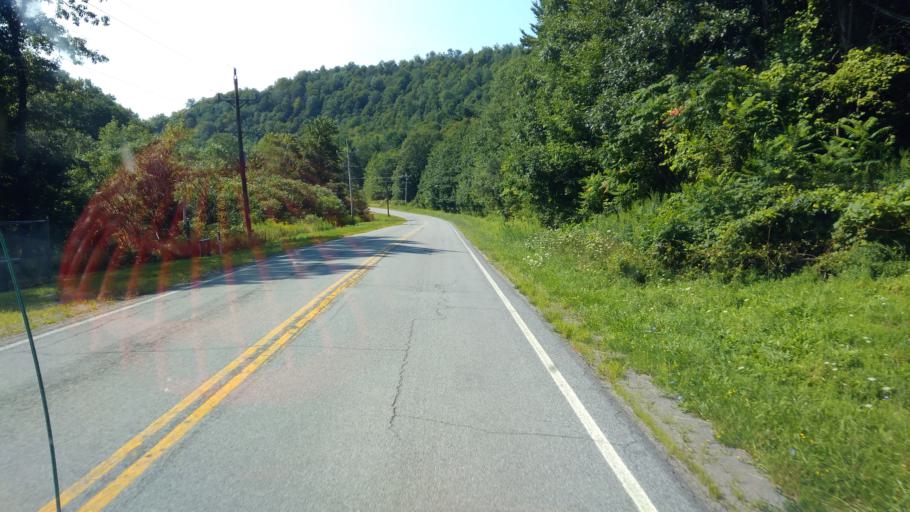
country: US
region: New York
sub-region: Allegany County
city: Bolivar
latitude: 42.1196
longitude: -78.1594
